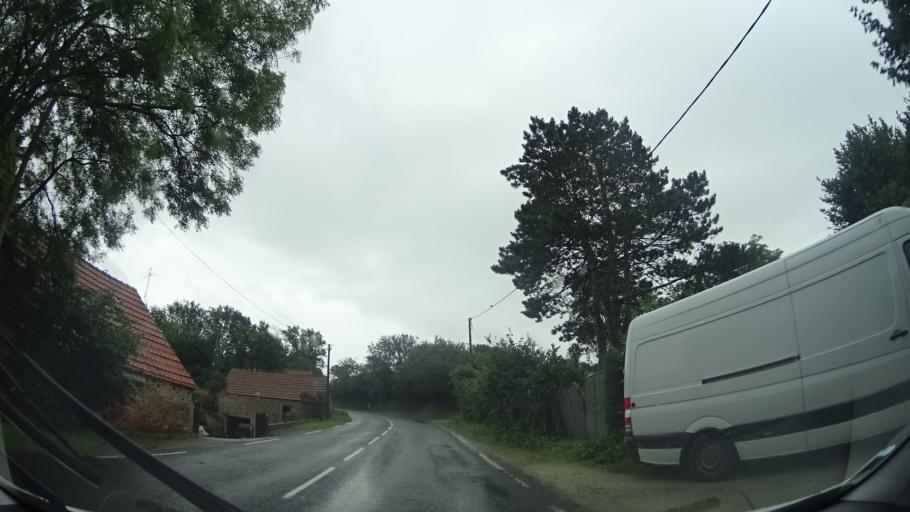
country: FR
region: Lower Normandy
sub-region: Departement de la Manche
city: Beaumont-Hague
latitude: 49.6073
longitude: -1.7900
